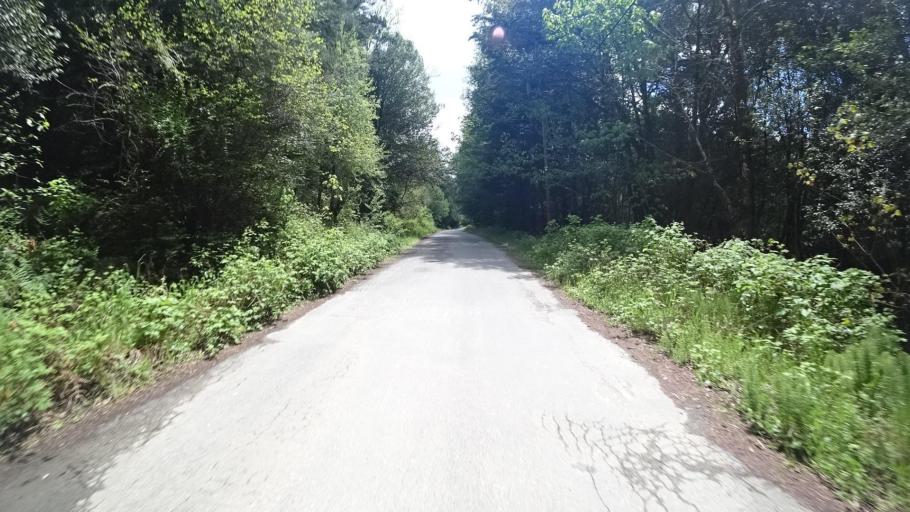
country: US
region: California
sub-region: Humboldt County
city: Blue Lake
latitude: 40.7774
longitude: -123.8773
